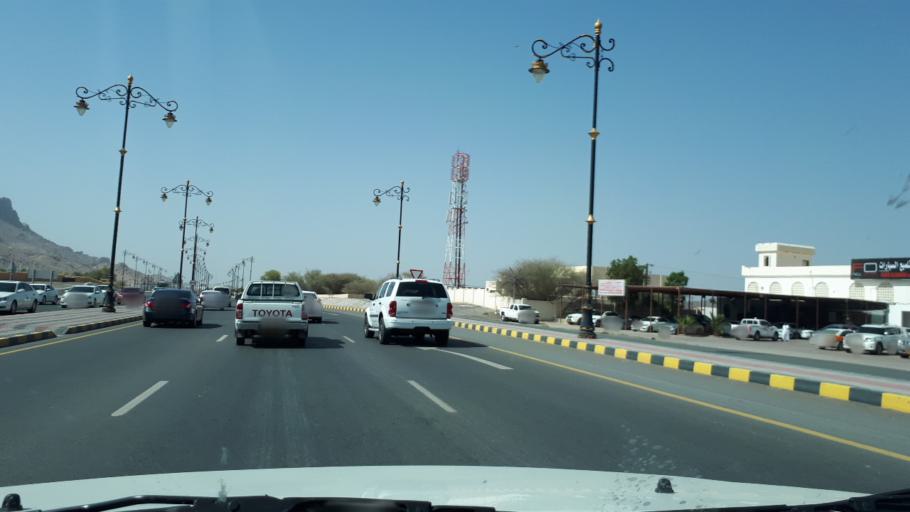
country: OM
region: Muhafazat ad Dakhiliyah
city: Nizwa
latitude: 22.9203
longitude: 57.5360
